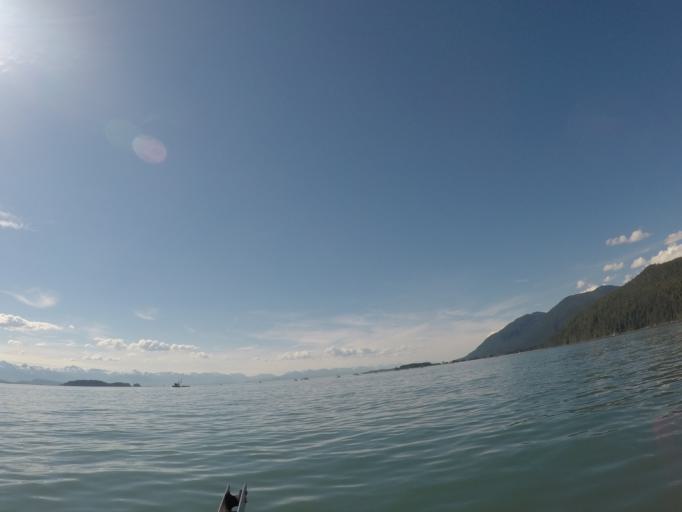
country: US
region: Alaska
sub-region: Juneau City and Borough
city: Juneau
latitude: 58.4941
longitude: -134.8148
